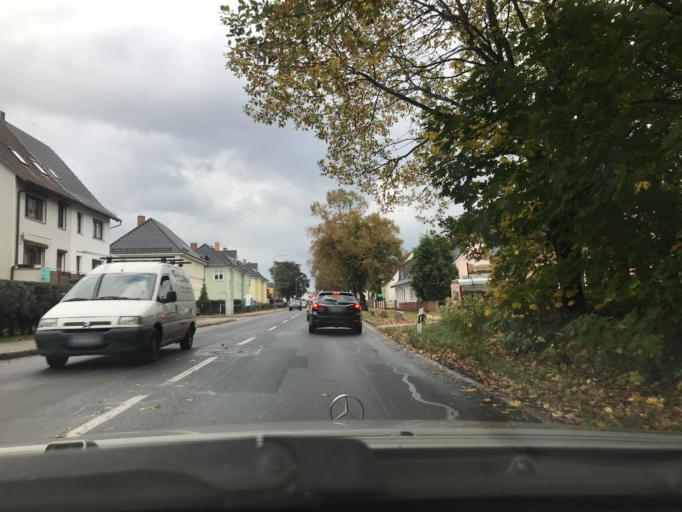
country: DE
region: Mecklenburg-Vorpommern
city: Seebad Heringsdorf
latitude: 53.9447
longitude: 14.1782
